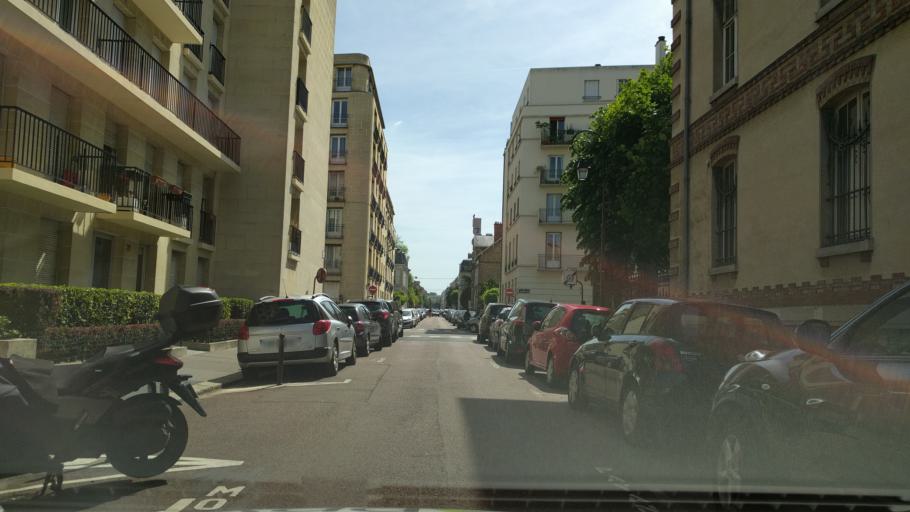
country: FR
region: Ile-de-France
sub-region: Departement des Yvelines
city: Versailles
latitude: 48.8109
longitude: 2.1340
